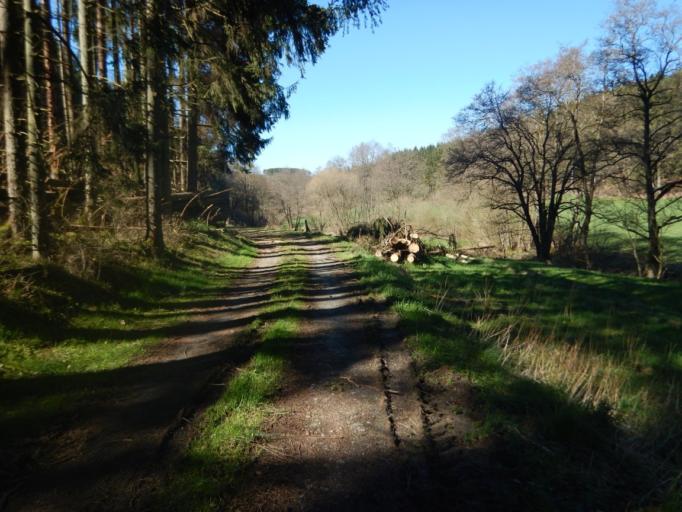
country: LU
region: Diekirch
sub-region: Canton de Wiltz
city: Eschweiler
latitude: 49.9844
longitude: 5.9687
